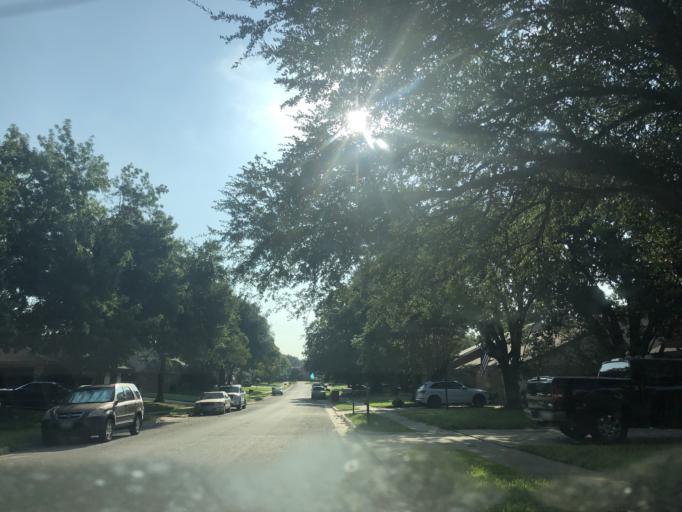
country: US
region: Texas
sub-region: Tarrant County
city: Euless
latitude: 32.8725
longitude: -97.0809
